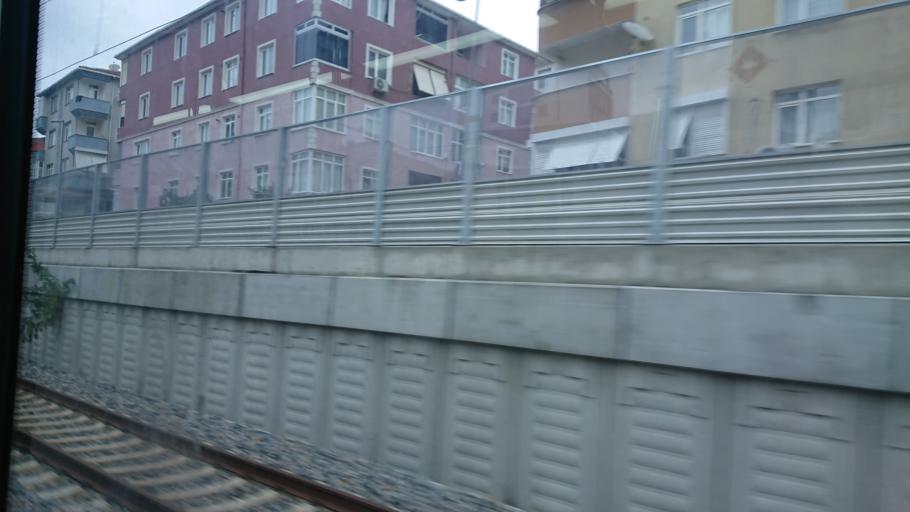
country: TR
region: Istanbul
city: Mahmutbey
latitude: 40.9969
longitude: 28.7676
